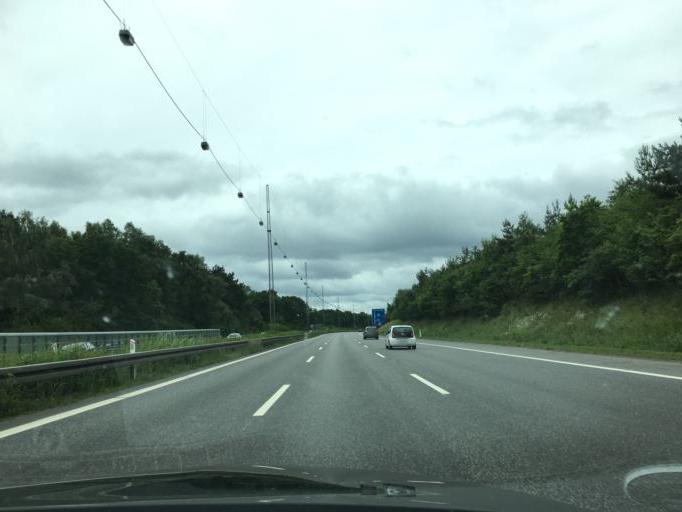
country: DK
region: Capital Region
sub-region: Rudersdal Kommune
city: Trorod
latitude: 55.8098
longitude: 12.5312
